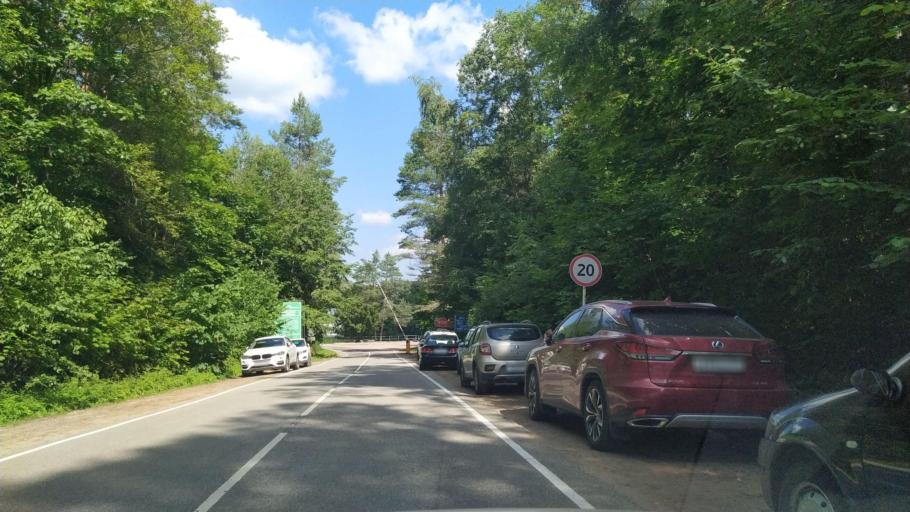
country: RU
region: Pskov
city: Pushkinskiye Gory
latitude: 57.0742
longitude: 28.9562
